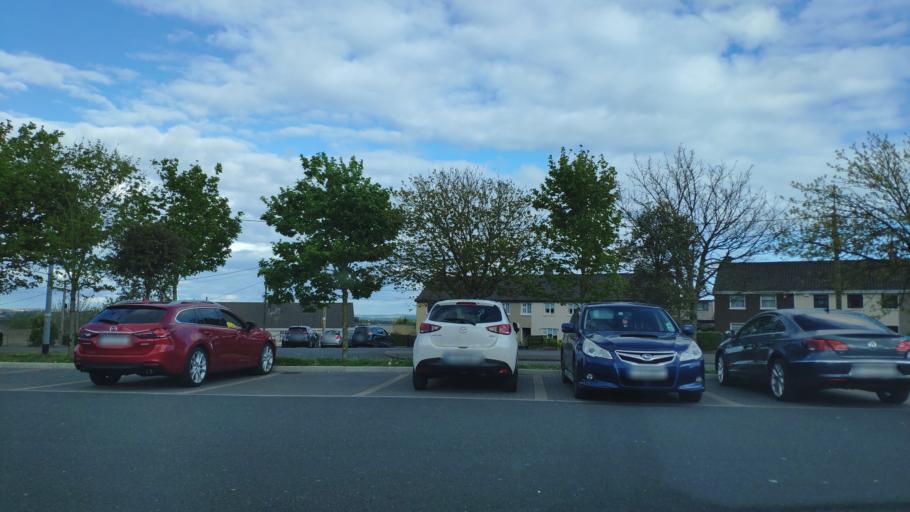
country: IE
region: Munster
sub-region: County Cork
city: Cork
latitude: 51.9117
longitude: -8.4899
